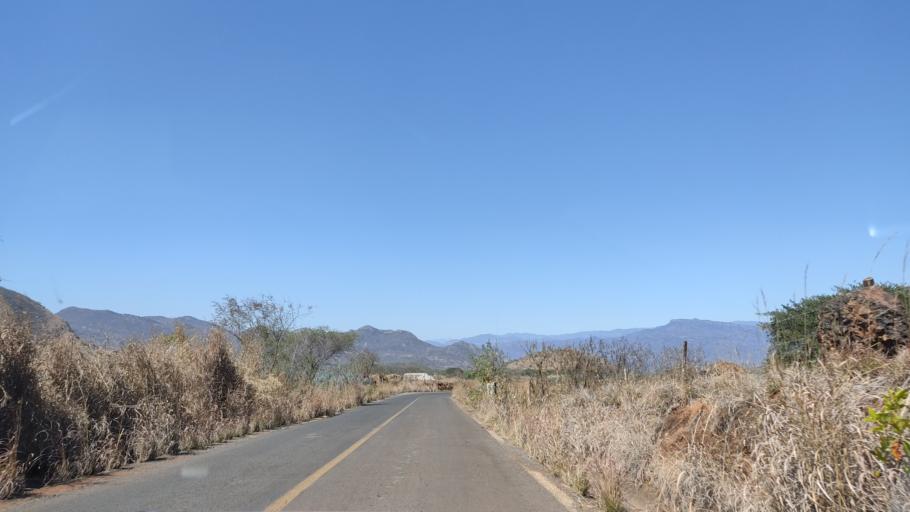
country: MX
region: Nayarit
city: Santa Maria del Oro
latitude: 21.4887
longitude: -104.6241
